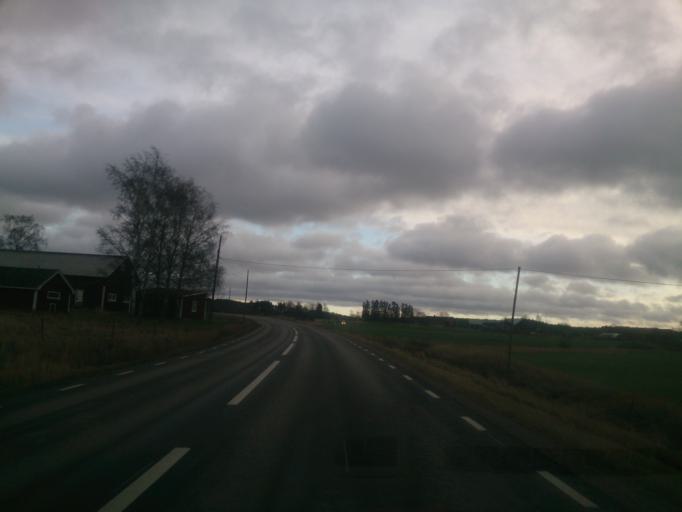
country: SE
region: OEstergoetland
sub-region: Norrkopings Kommun
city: Krokek
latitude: 58.5708
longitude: 16.4217
